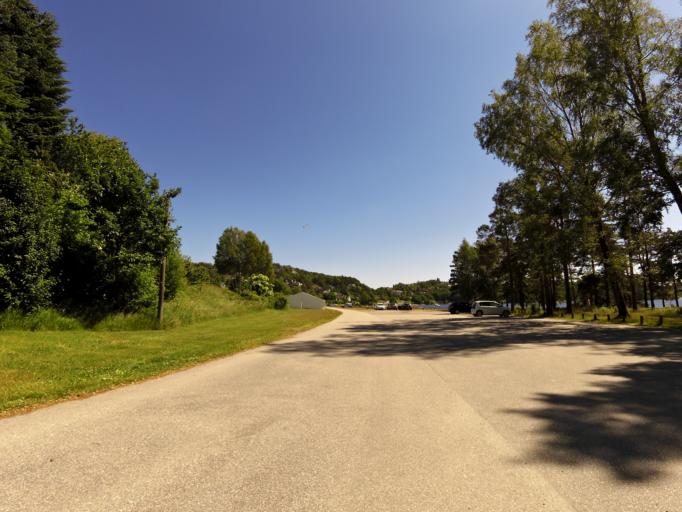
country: NO
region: Vest-Agder
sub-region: Kristiansand
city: Justvik
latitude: 58.1916
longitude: 8.0807
